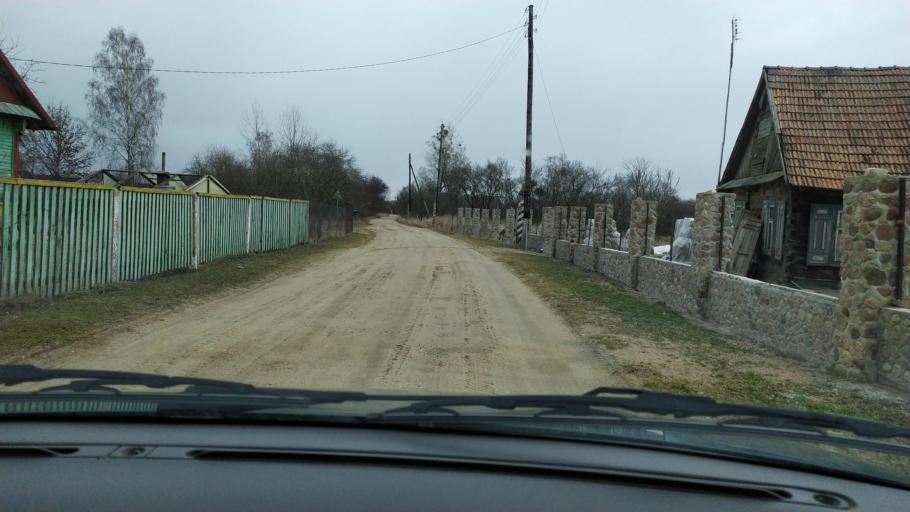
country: BY
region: Brest
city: Kamyanyets
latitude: 52.4117
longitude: 24.0161
